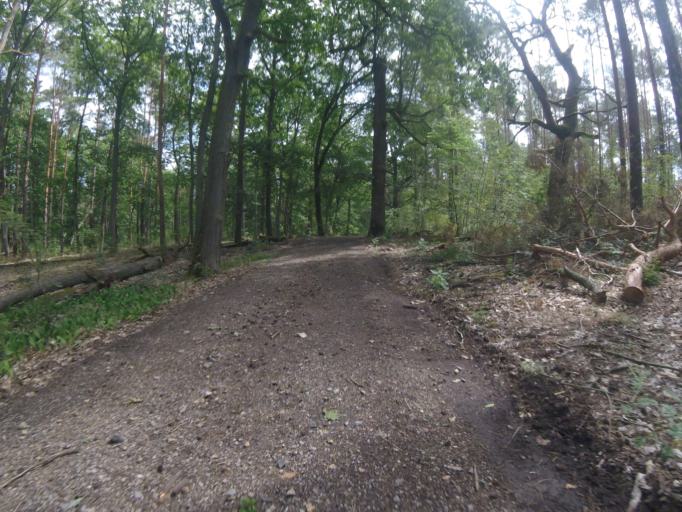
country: DE
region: Brandenburg
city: Gross Koris
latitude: 52.1976
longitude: 13.6897
